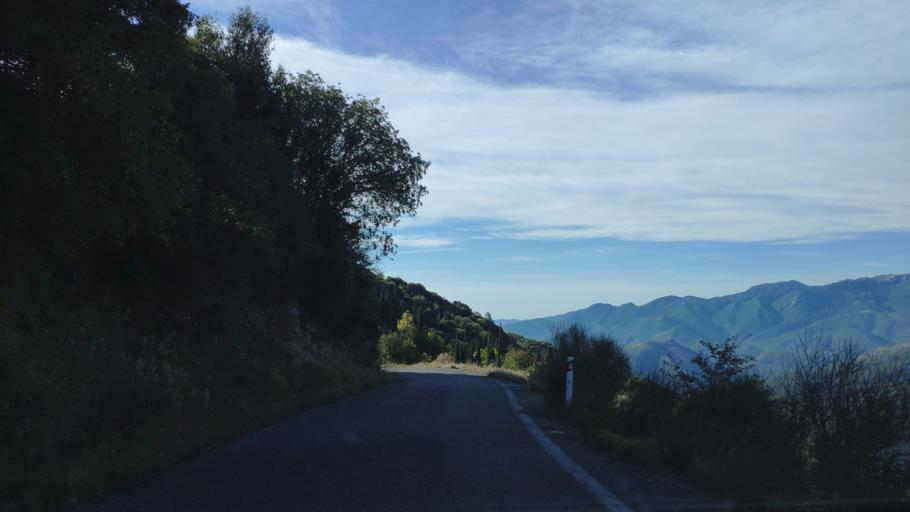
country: GR
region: Peloponnese
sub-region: Nomos Arkadias
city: Dimitsana
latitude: 37.5563
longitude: 22.0597
